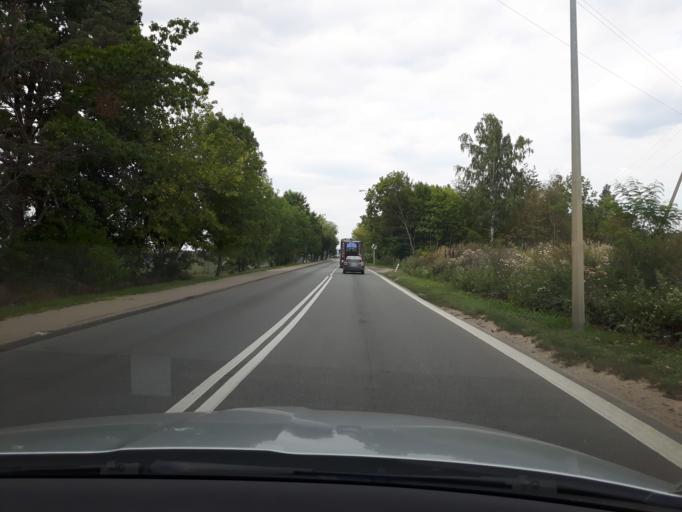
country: PL
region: Masovian Voivodeship
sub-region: Warszawa
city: Targowek
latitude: 52.3305
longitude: 21.0308
